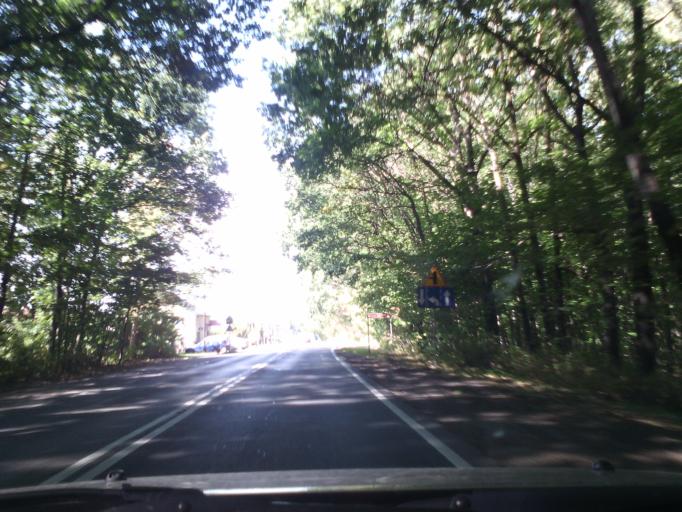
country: PL
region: Silesian Voivodeship
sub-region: Powiat rybnicki
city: Szczerbice
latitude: 50.0794
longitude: 18.4656
